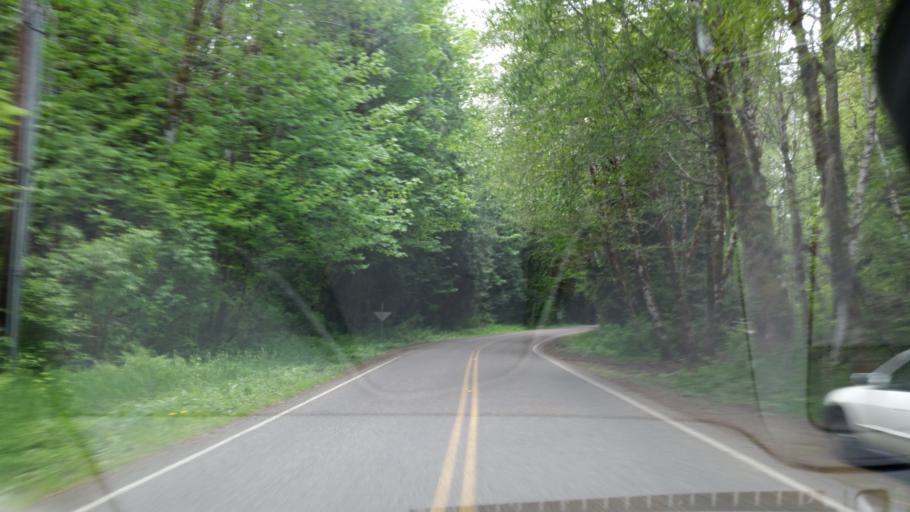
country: US
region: Washington
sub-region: Mason County
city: Shelton
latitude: 47.3155
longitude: -123.2524
